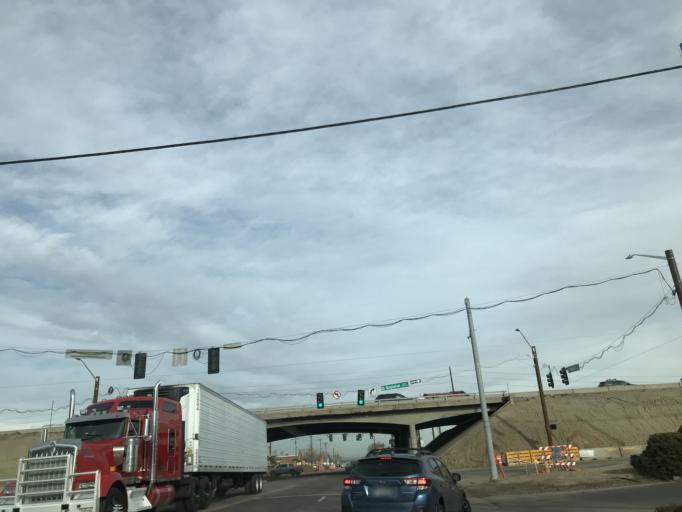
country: US
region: Colorado
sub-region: Adams County
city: Commerce City
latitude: 39.7777
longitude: -104.9129
